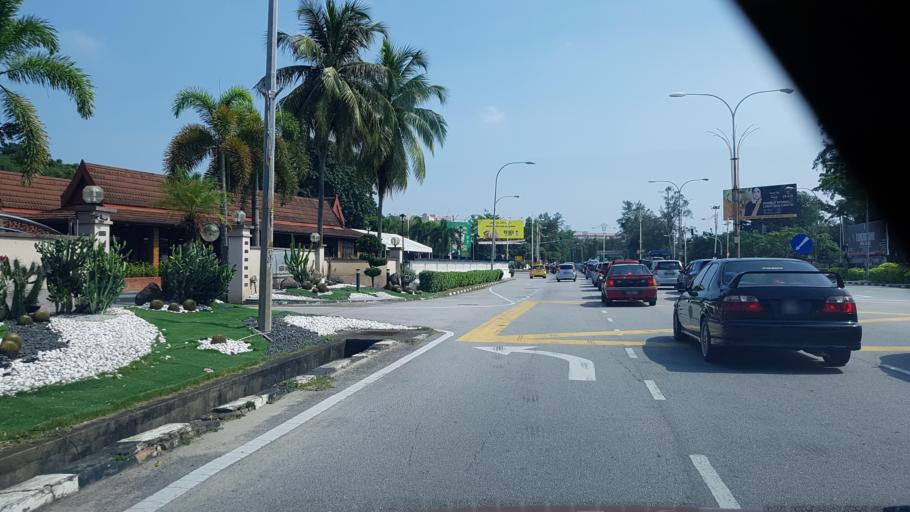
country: MY
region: Terengganu
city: Kuala Terengganu
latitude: 5.3179
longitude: 103.1536
